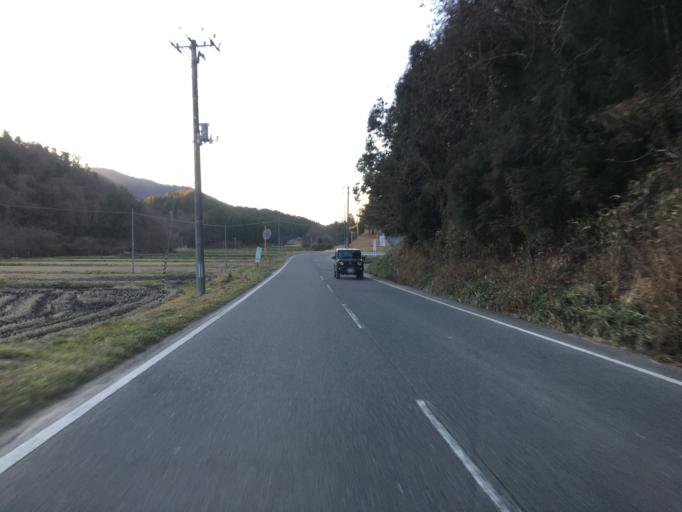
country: JP
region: Fukushima
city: Ishikawa
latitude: 37.2729
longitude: 140.5732
